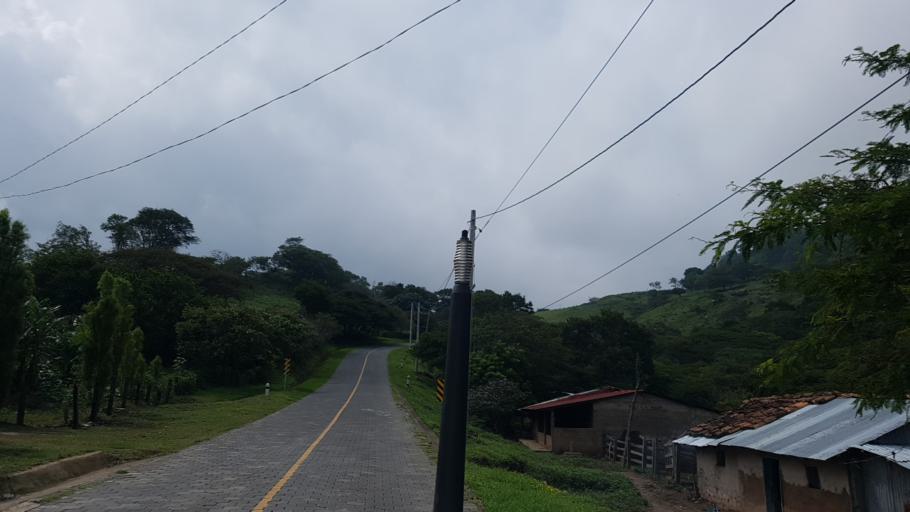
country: NI
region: Leon
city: Santa Rosa del Penon
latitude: 12.9406
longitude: -86.3414
